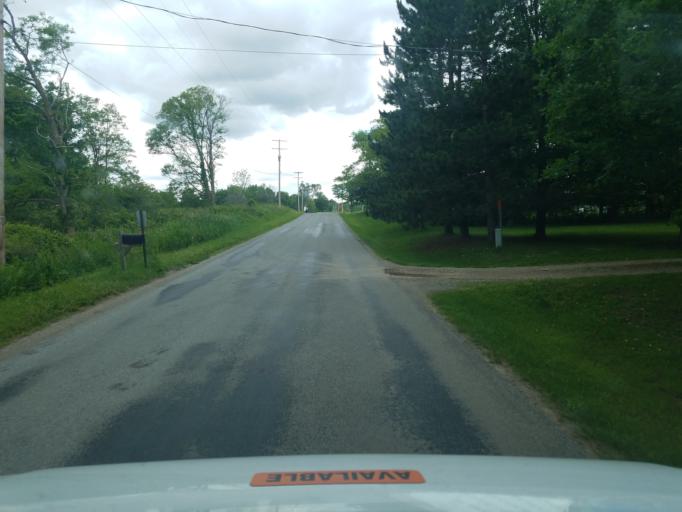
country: US
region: Ohio
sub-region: Crawford County
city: Crestline
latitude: 40.7169
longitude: -82.6891
